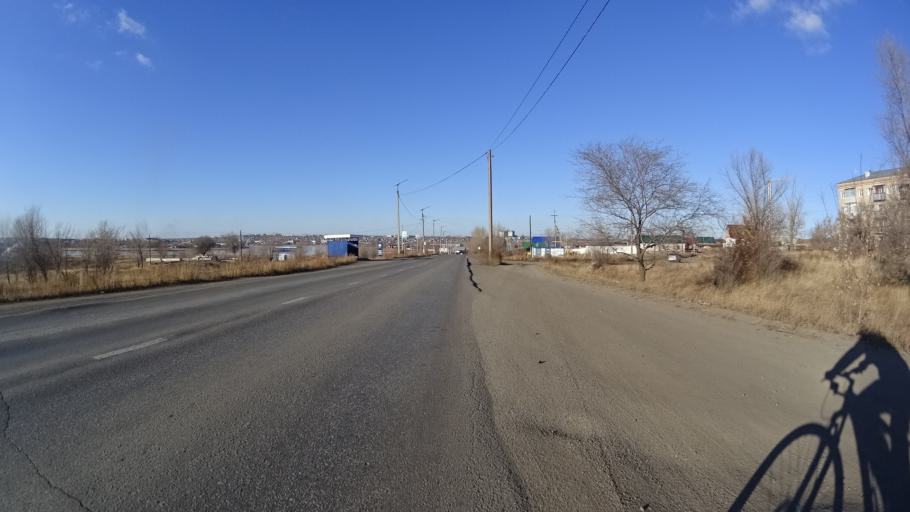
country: RU
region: Chelyabinsk
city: Troitsk
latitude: 54.0818
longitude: 61.5968
